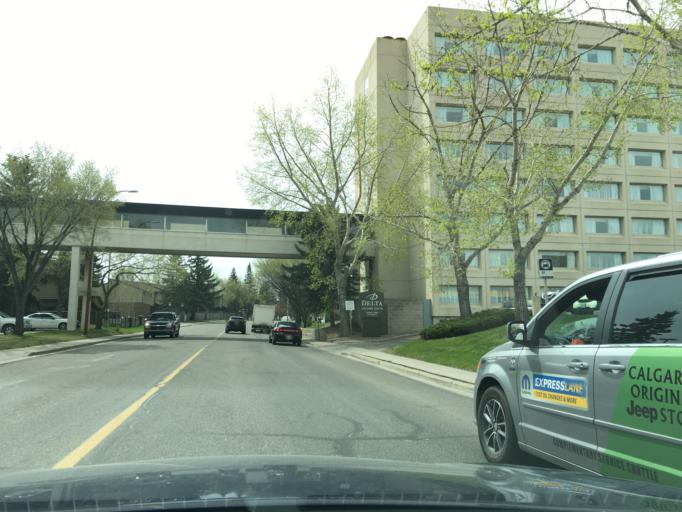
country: CA
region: Alberta
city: Calgary
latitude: 50.9648
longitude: -114.0681
